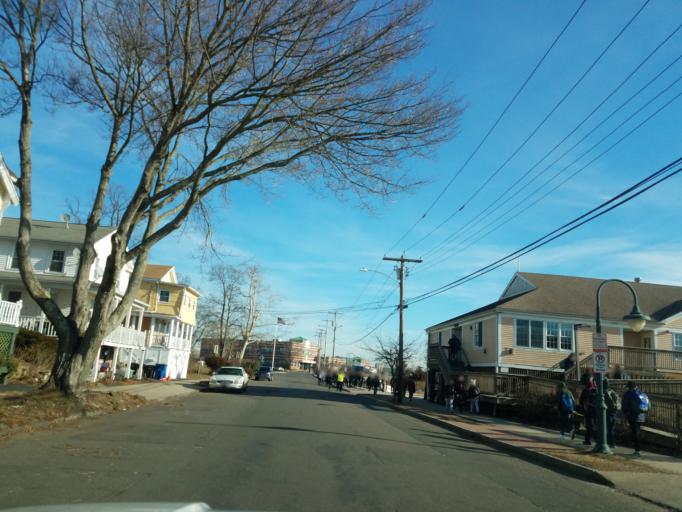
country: US
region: Connecticut
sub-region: New Haven County
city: West Haven
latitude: 41.2824
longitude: -72.9283
